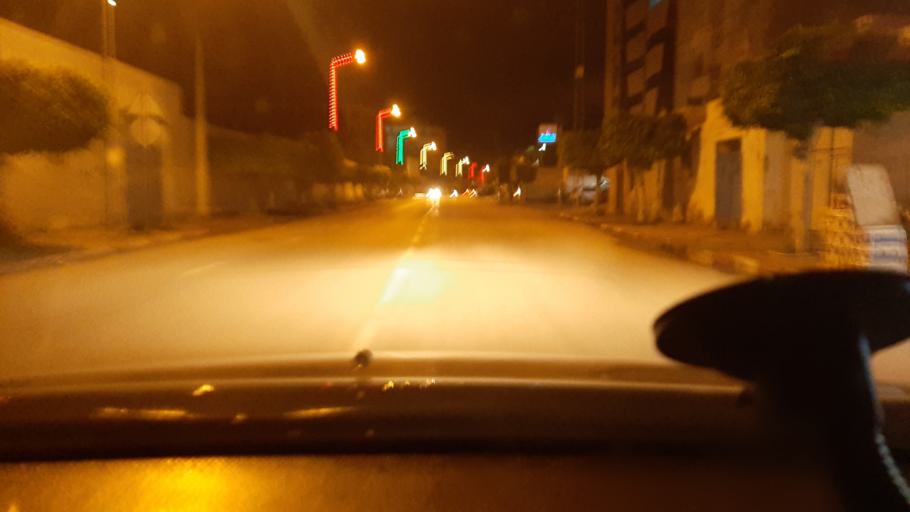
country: TN
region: Safaqis
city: Sfax
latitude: 34.7845
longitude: 10.7215
